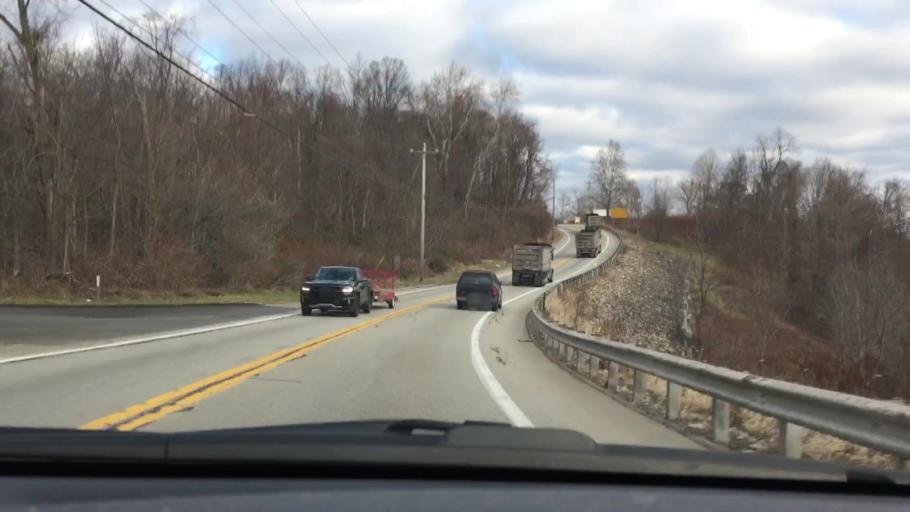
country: US
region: Pennsylvania
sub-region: Westmoreland County
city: Trafford
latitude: 40.3796
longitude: -79.7769
